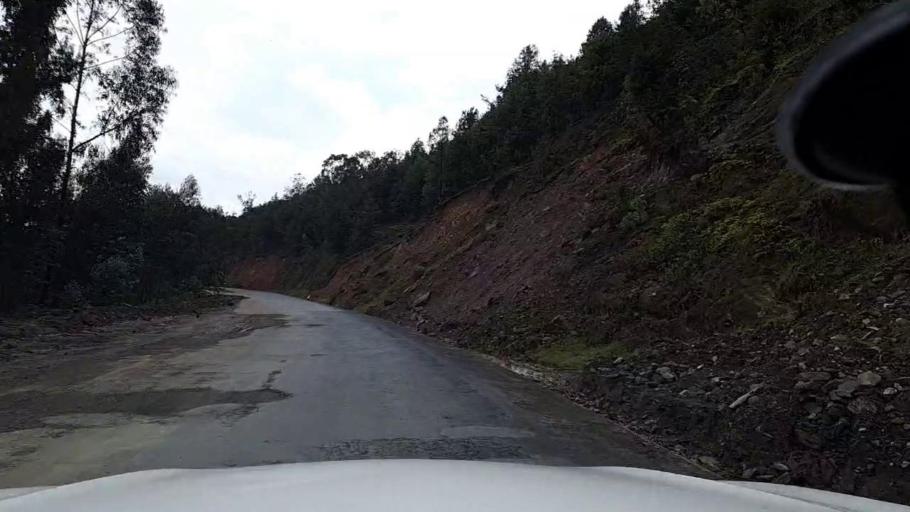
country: RW
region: Western Province
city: Kibuye
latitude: -2.0614
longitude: 29.5293
